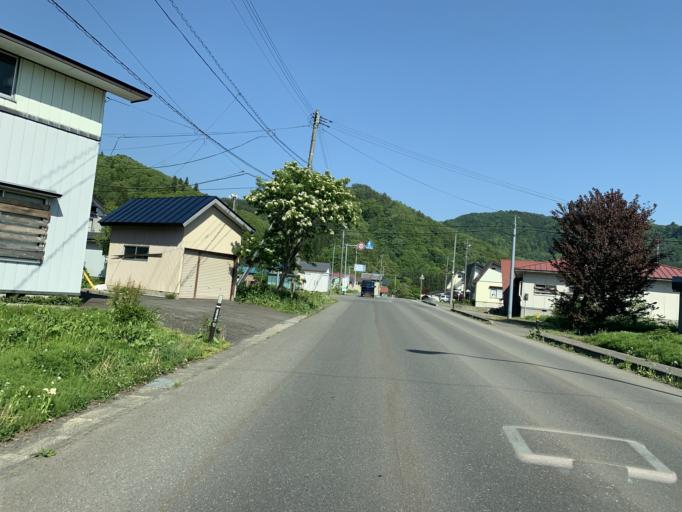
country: JP
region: Akita
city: Yokotemachi
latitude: 39.3363
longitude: 140.7828
